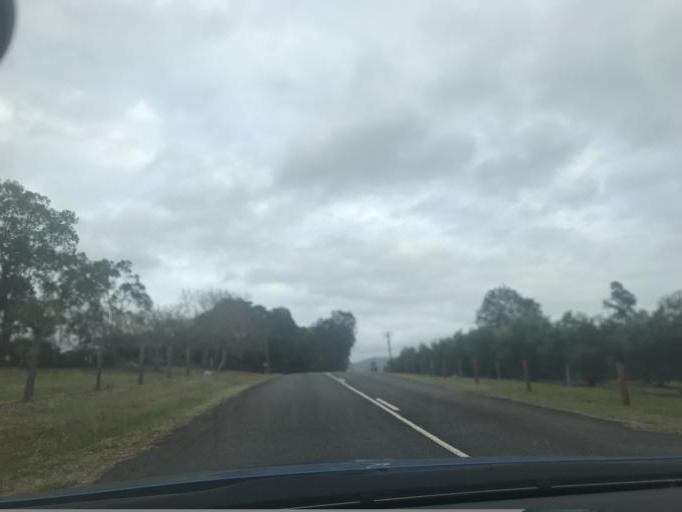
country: AU
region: New South Wales
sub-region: Cessnock
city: Cessnock
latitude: -32.8132
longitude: 151.3213
